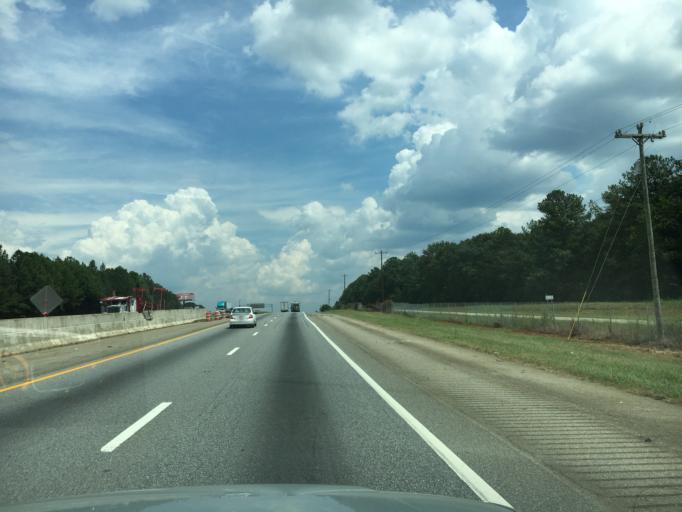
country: US
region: South Carolina
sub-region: Spartanburg County
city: Mayo
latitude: 35.0287
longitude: -81.8670
